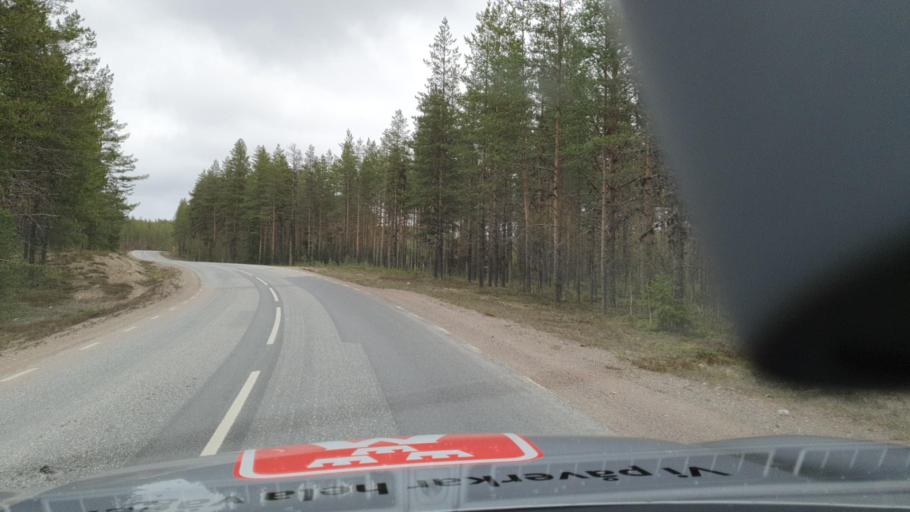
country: SE
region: Vaesternorrland
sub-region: Solleftea Kommun
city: Solleftea
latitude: 63.6409
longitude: 17.4046
